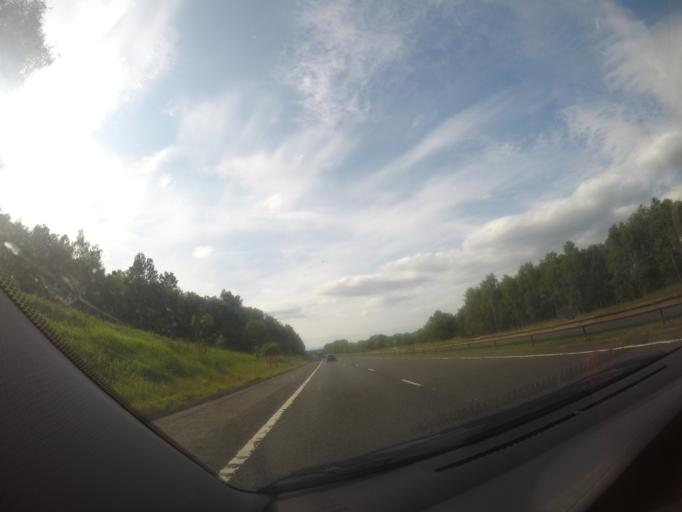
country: GB
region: Scotland
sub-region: South Lanarkshire
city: Larkhall
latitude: 55.7542
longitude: -3.9706
